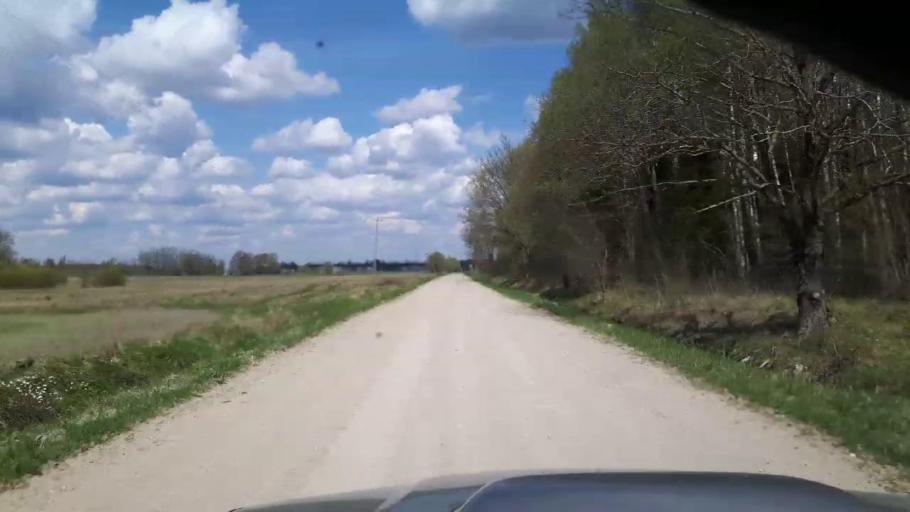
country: EE
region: Paernumaa
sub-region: Tootsi vald
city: Tootsi
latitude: 58.4815
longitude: 24.9016
